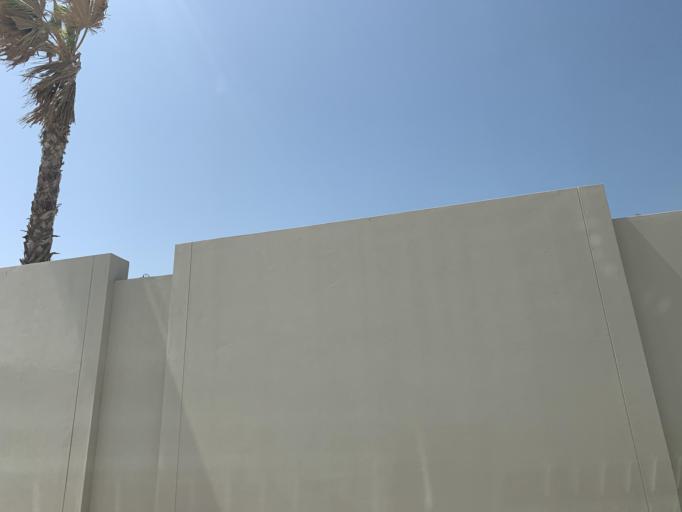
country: BH
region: Northern
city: Madinat `Isa
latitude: 26.1553
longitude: 50.5519
